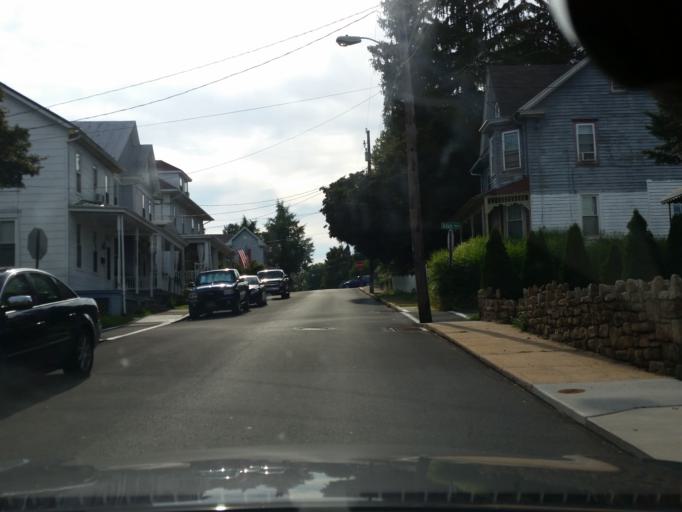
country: US
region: Pennsylvania
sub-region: Perry County
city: Marysville
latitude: 40.3424
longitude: -76.9326
